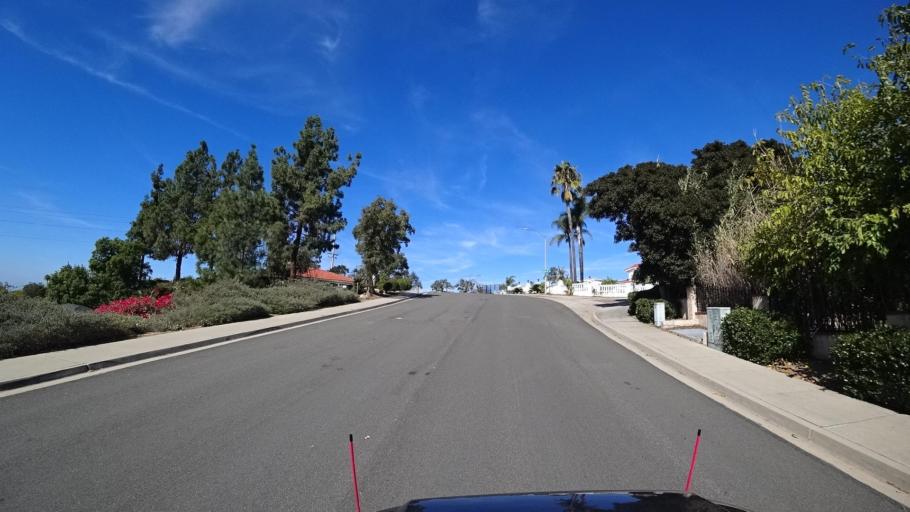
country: US
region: California
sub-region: San Diego County
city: Casa de Oro-Mount Helix
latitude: 32.7563
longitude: -116.9526
